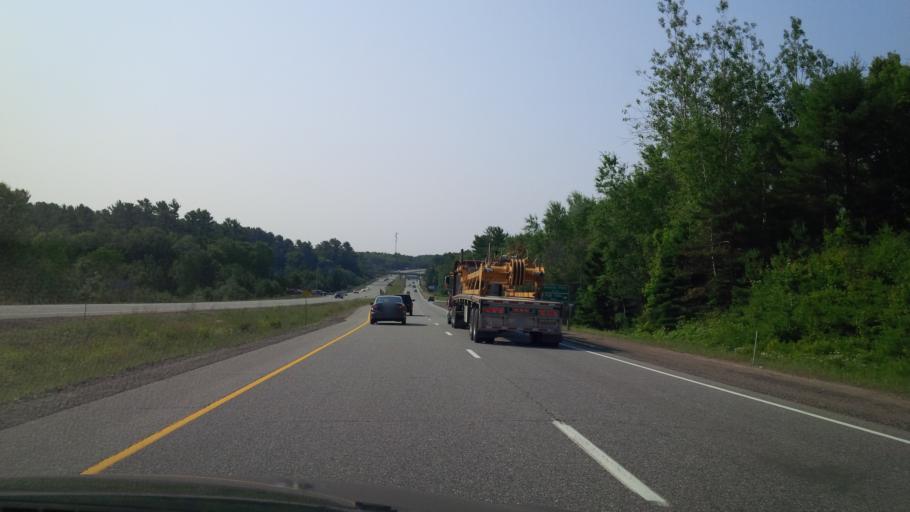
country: CA
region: Ontario
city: Bracebridge
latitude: 45.0932
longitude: -79.3031
